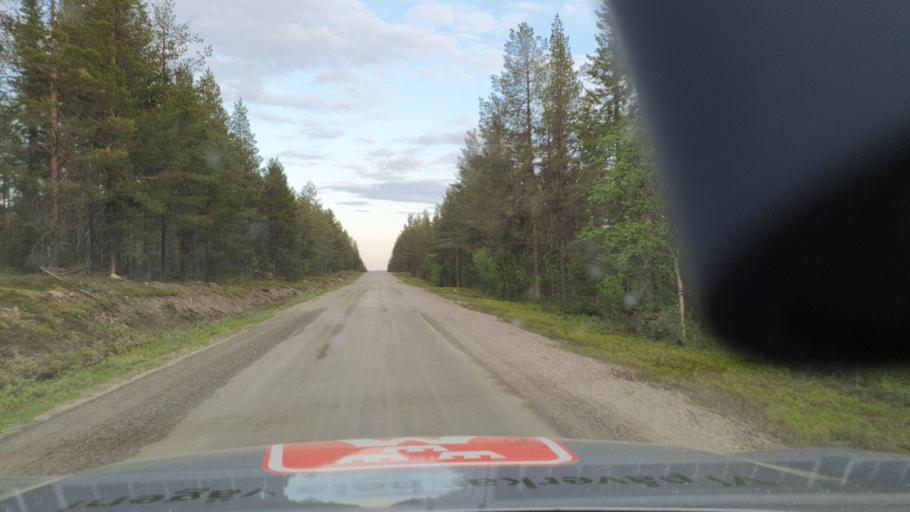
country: SE
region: Norrbotten
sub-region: Gallivare Kommun
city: Gaellivare
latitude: 66.6226
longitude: 21.3431
